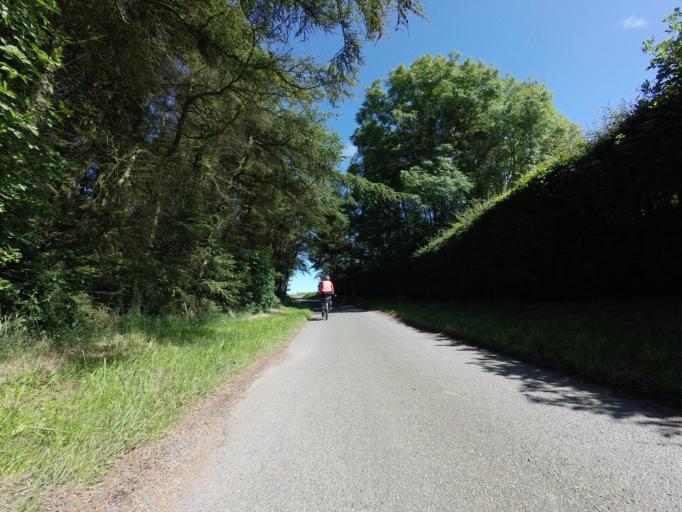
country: GB
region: Scotland
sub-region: Aberdeenshire
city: Banff
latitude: 57.6172
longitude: -2.5091
